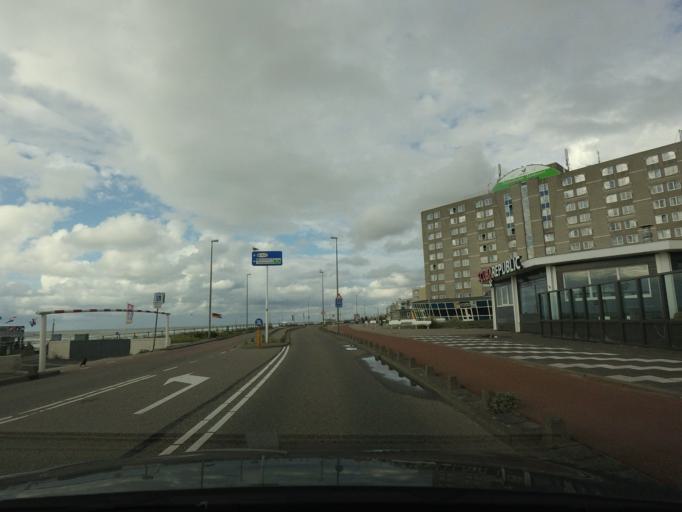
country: NL
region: North Holland
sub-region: Gemeente Zandvoort
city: Zandvoort
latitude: 52.3795
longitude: 4.5297
